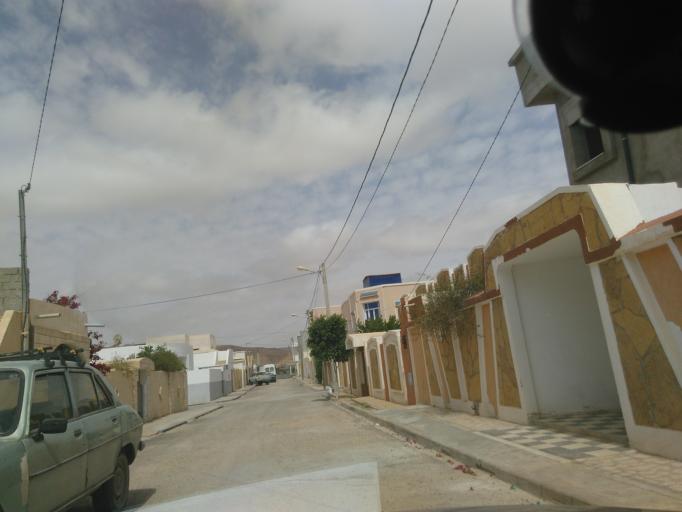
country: TN
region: Tataouine
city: Tataouine
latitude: 32.9515
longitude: 10.4655
